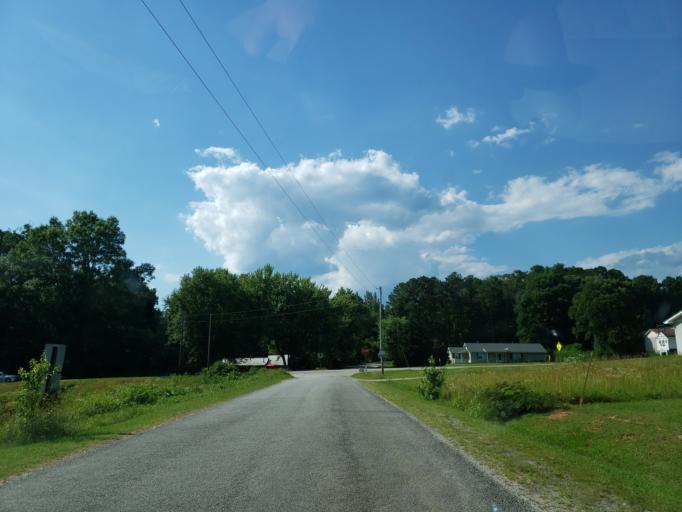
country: US
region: Georgia
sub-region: Haralson County
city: Buchanan
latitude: 33.8186
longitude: -85.0909
